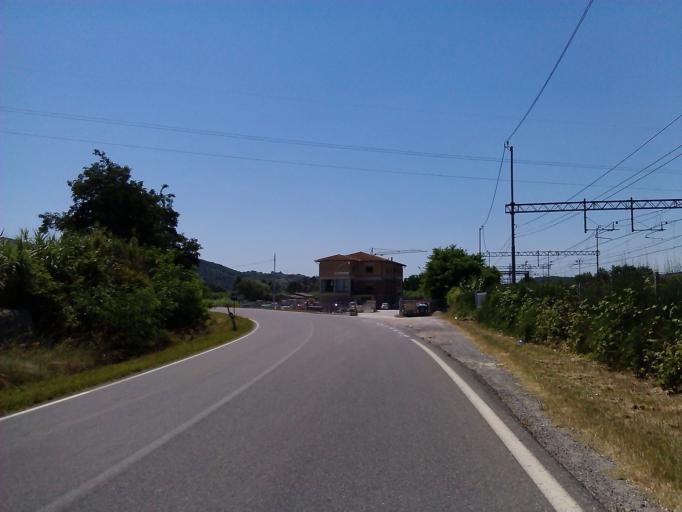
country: IT
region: Umbria
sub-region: Provincia di Terni
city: Fabro Scalo
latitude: 42.8712
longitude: 12.0420
